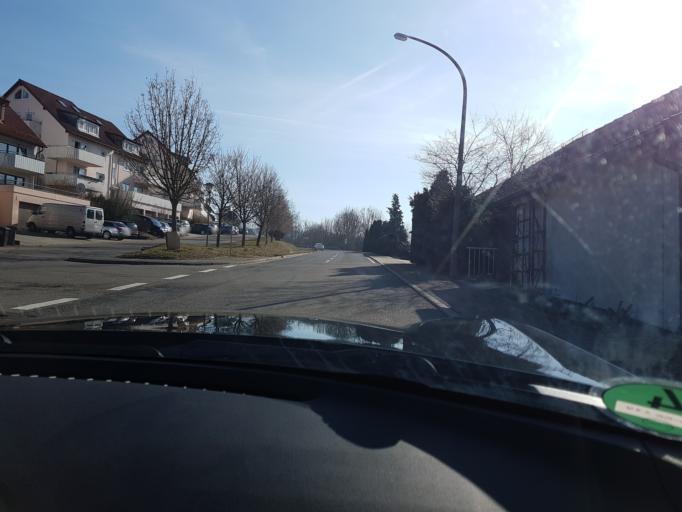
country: DE
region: Baden-Wuerttemberg
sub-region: Regierungsbezirk Stuttgart
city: Mulfingen
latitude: 49.3378
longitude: 9.8023
